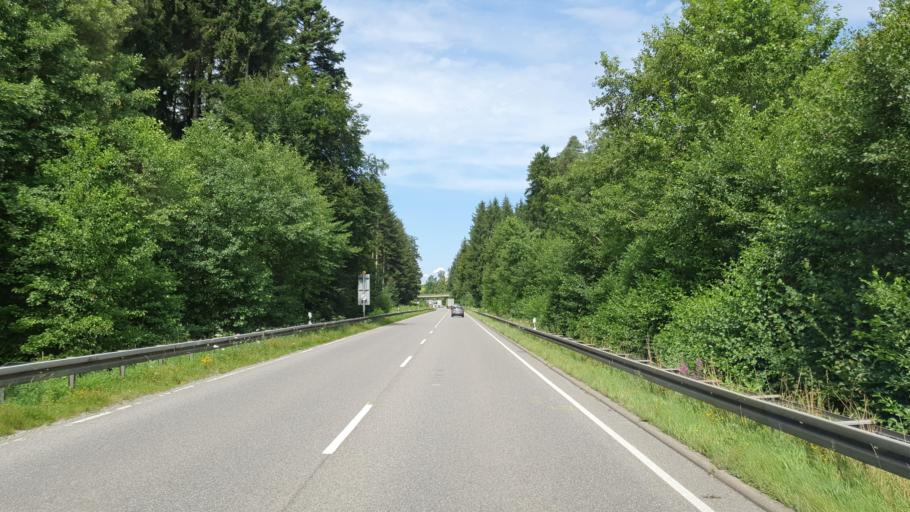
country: DE
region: Bavaria
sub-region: Swabia
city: Bodolz
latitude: 47.5919
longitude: 9.6437
